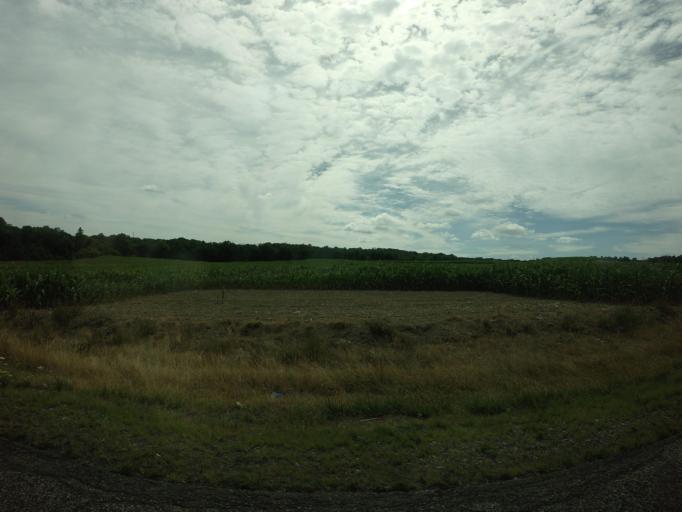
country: US
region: New York
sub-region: Onondaga County
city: Camillus
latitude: 43.0342
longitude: -76.3043
